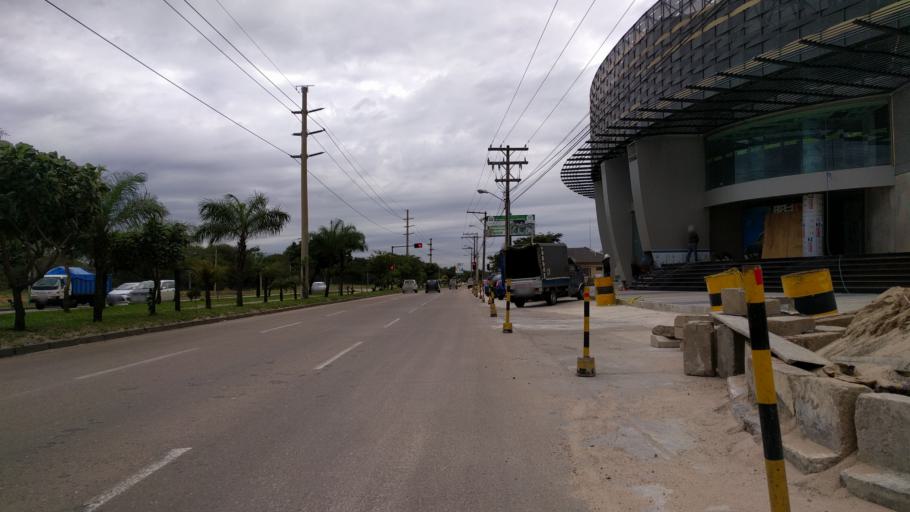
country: BO
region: Santa Cruz
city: Santa Cruz de la Sierra
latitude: -17.7605
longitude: -63.2022
